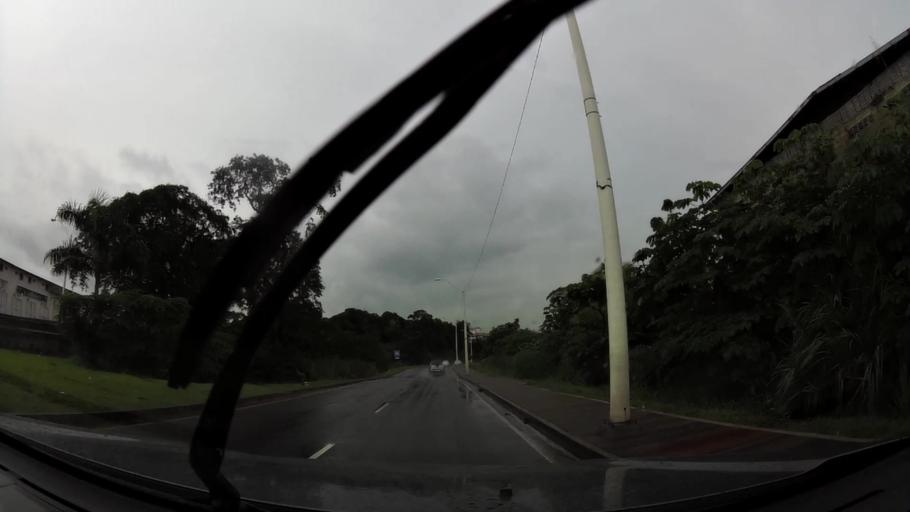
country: PA
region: Colon
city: Arco Iris
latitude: 9.3414
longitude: -79.8897
